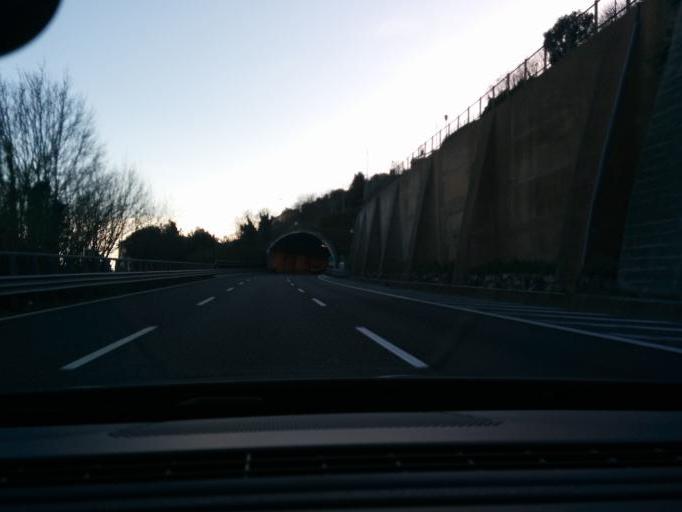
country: IT
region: Liguria
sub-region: Provincia di Genova
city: Mele
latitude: 44.4209
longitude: 8.7271
